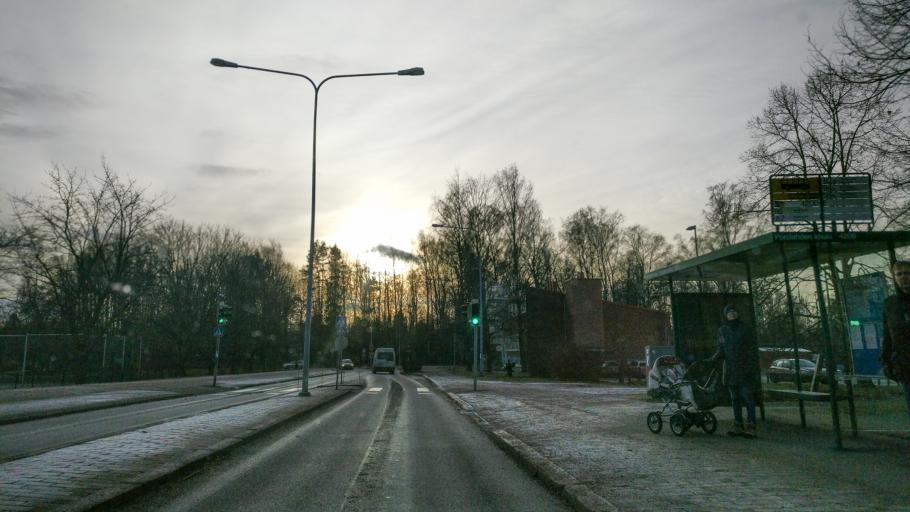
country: FI
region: Uusimaa
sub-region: Helsinki
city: Vantaa
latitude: 60.1954
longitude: 25.0534
